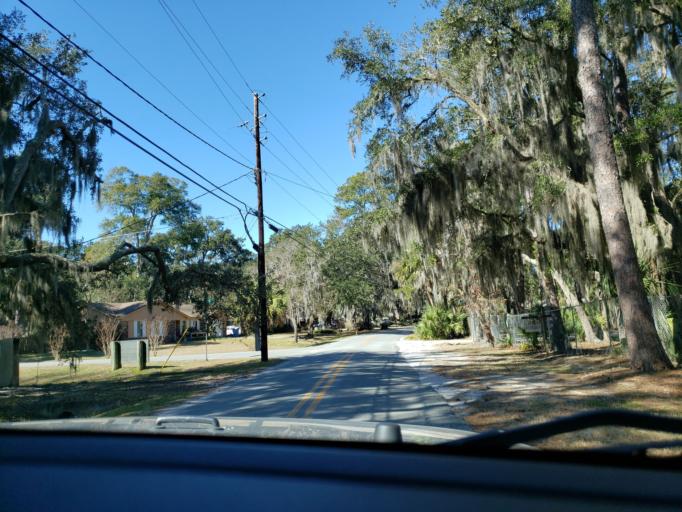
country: US
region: Georgia
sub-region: Chatham County
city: Whitemarsh Island
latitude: 32.0420
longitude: -80.9950
